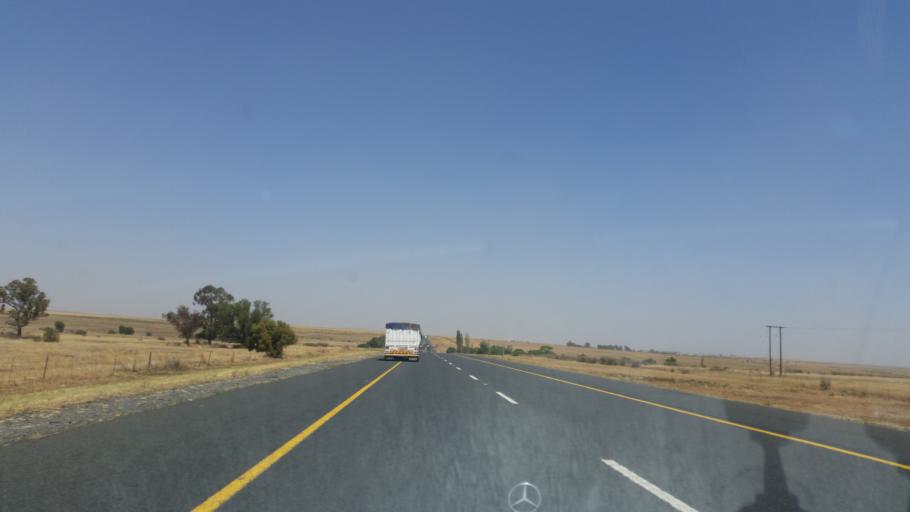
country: ZA
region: Orange Free State
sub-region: Lejweleputswa District Municipality
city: Brandfort
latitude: -28.7300
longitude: 26.7629
